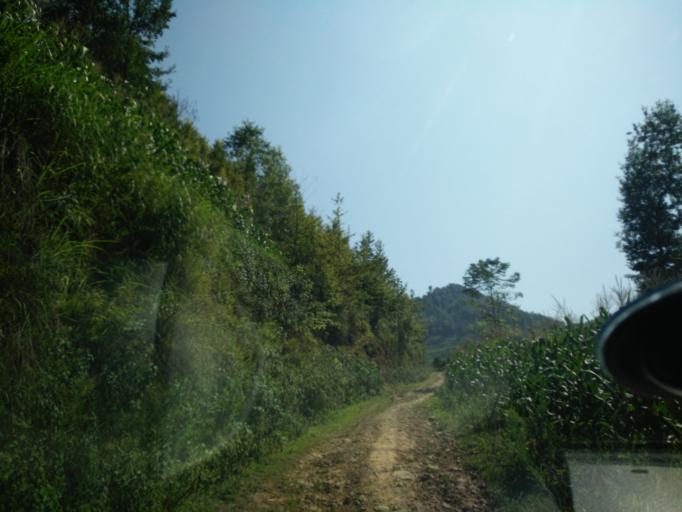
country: CN
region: Guangxi Zhuangzu Zizhiqu
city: Xinzhou
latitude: 25.1852
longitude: 105.6909
